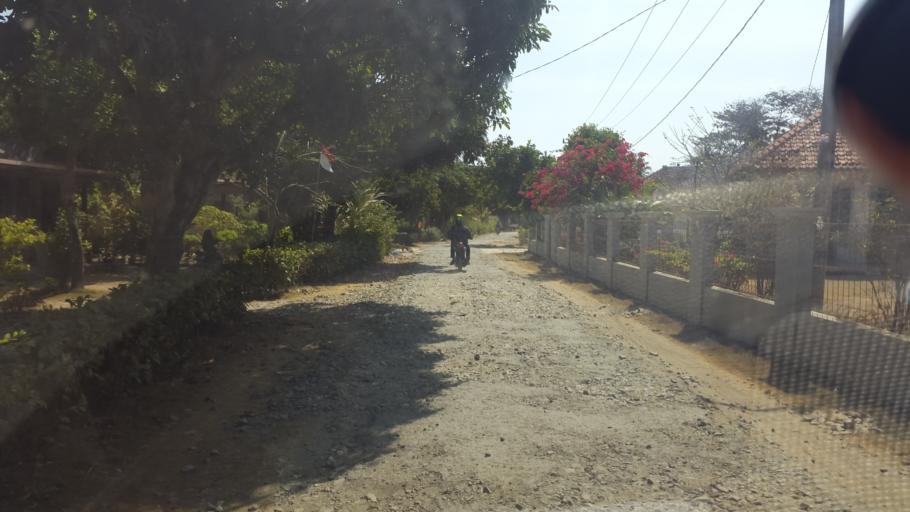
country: ID
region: West Java
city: Gunungbatu
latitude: -7.3431
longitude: 106.4034
